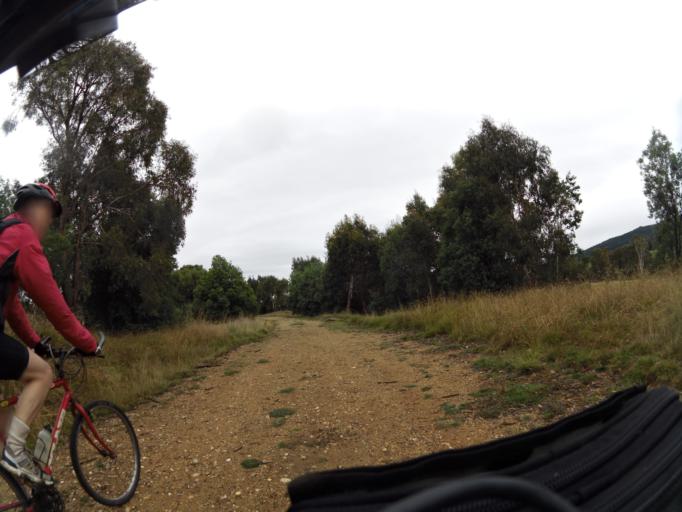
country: AU
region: New South Wales
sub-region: Greater Hume Shire
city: Holbrook
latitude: -36.1540
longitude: 147.4870
